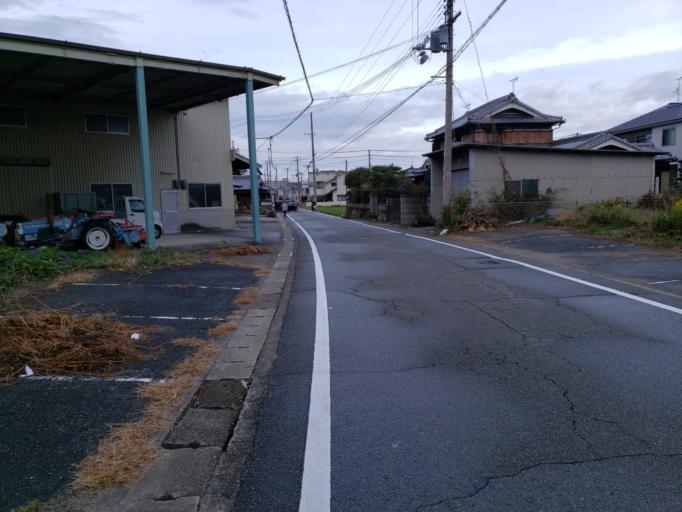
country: JP
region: Hyogo
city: Kakogawacho-honmachi
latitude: 34.7567
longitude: 134.8456
